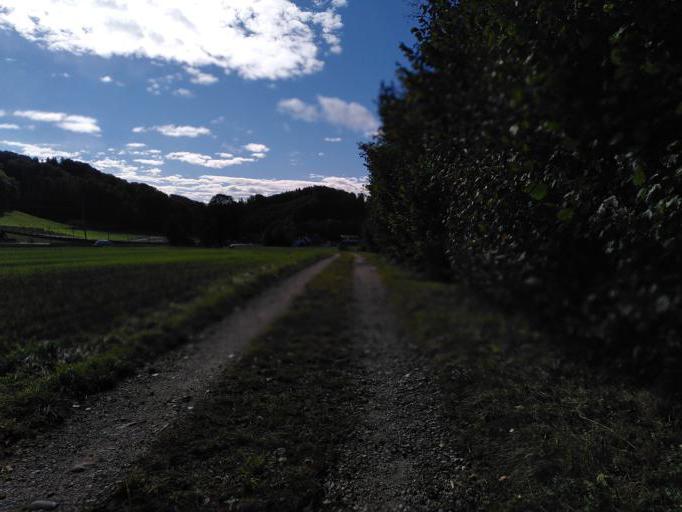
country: CH
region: Bern
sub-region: Oberaargau
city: Seeberg
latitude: 47.1492
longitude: 7.6934
